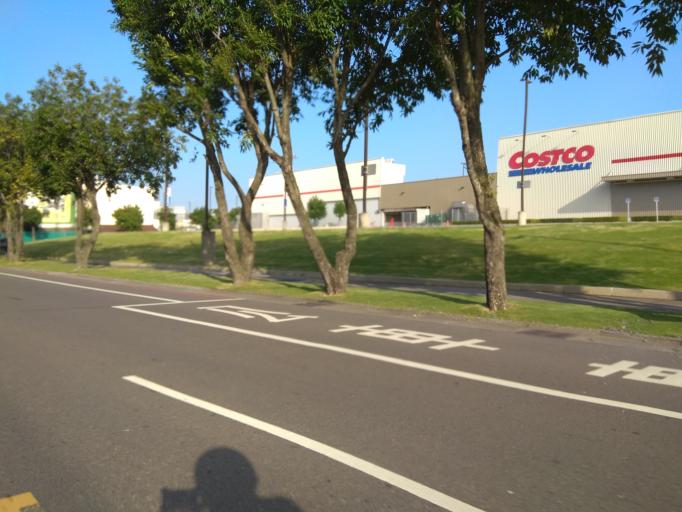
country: TW
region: Taiwan
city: Taoyuan City
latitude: 24.9630
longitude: 121.1557
